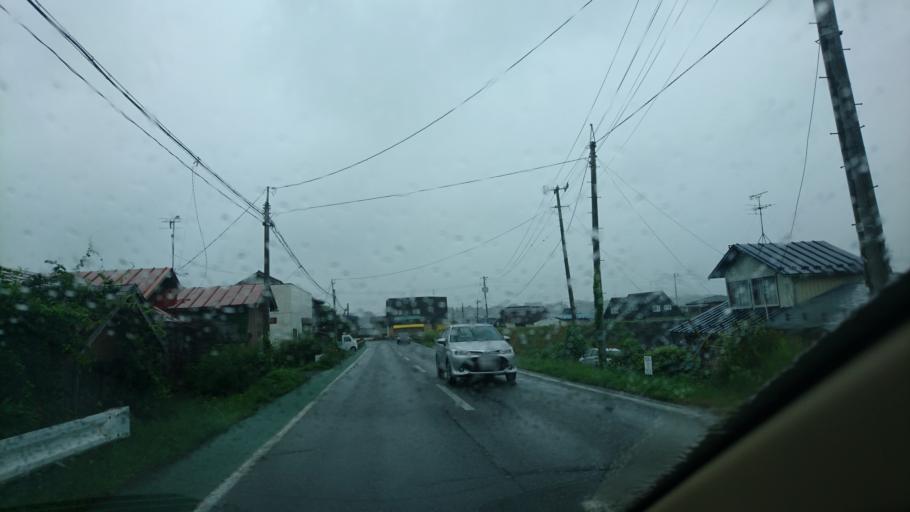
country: JP
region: Iwate
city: Kitakami
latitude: 39.2748
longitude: 141.1122
